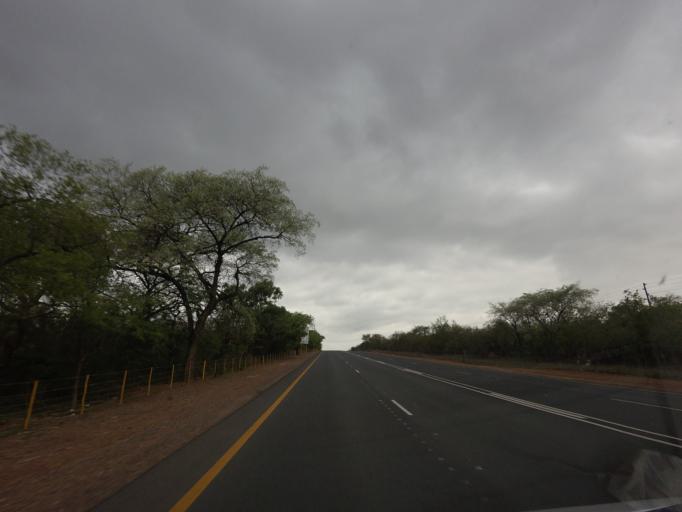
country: ZA
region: Mpumalanga
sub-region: Ehlanzeni District
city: Komatipoort
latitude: -25.4399
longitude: 31.7682
